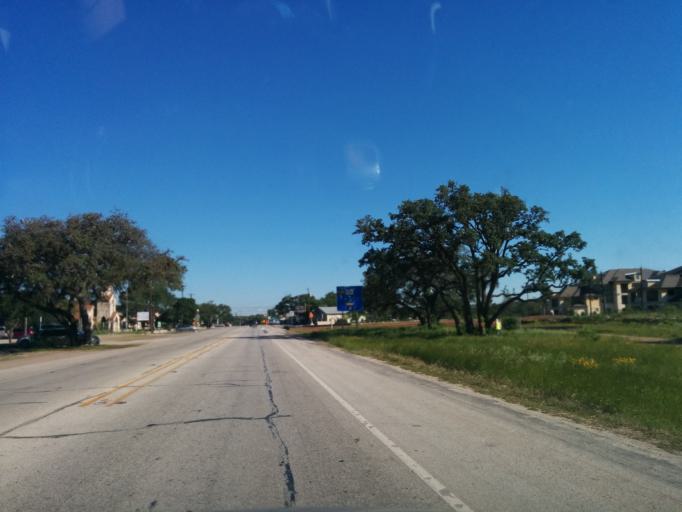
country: US
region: Texas
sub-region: Bexar County
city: Cross Mountain
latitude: 29.6629
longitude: -98.6281
